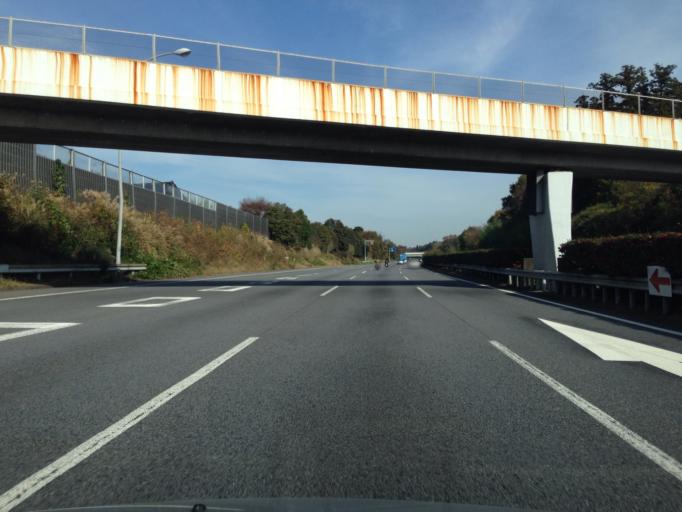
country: JP
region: Ibaraki
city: Ishioka
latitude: 36.1492
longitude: 140.2141
